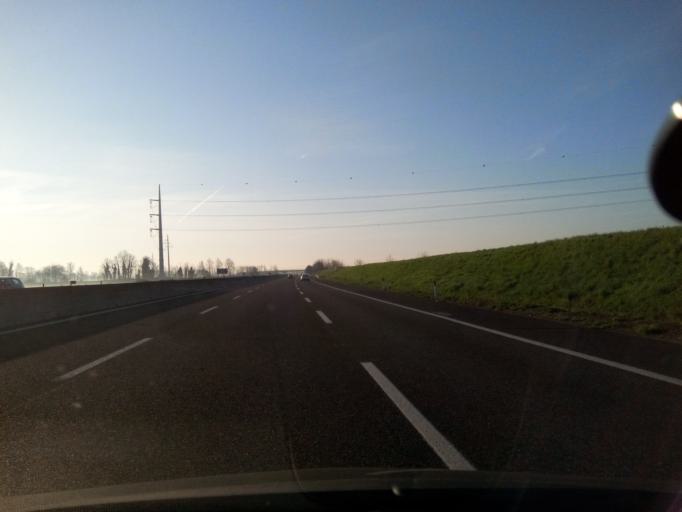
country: IT
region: Lombardy
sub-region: Provincia di Lodi
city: Fombio
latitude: 45.1261
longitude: 9.6646
